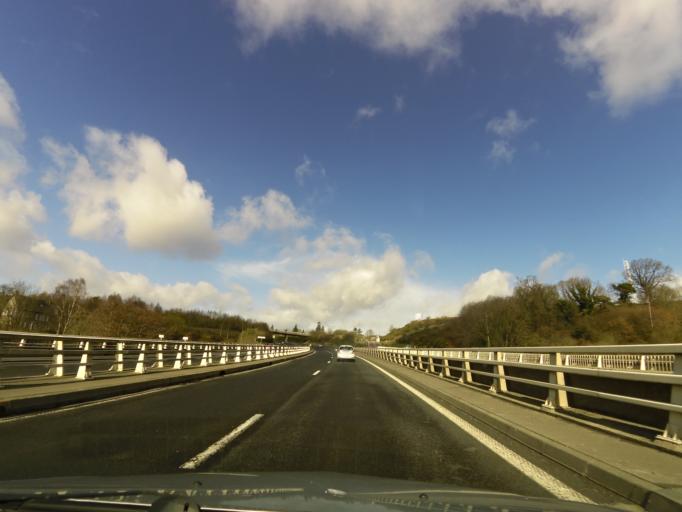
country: FR
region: Lower Normandy
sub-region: Departement de la Manche
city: Agneaux
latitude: 49.1097
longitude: -1.1211
